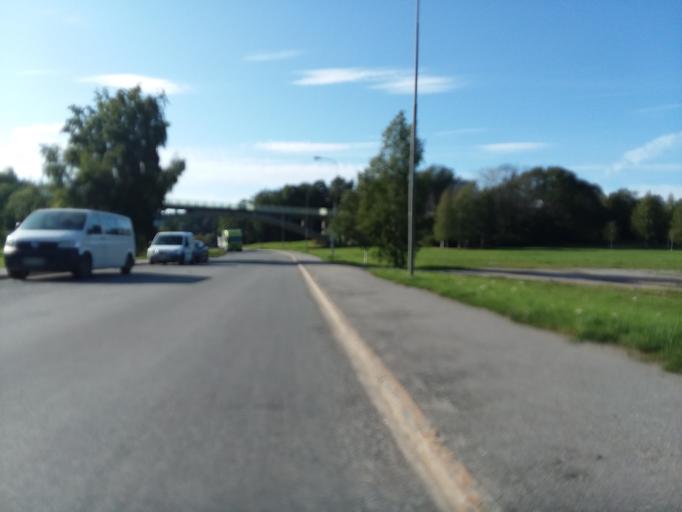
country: SE
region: Stockholm
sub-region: Stockholms Kommun
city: Bromma
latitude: 59.3514
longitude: 17.8833
